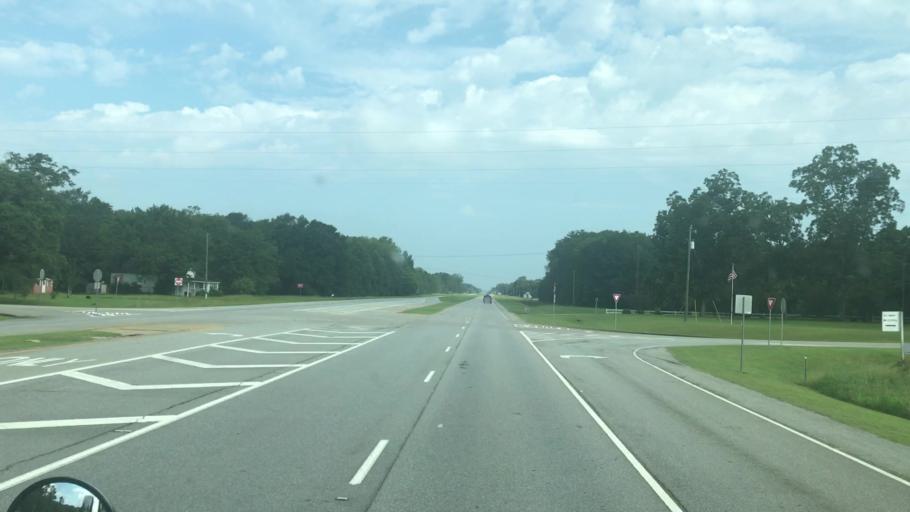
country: US
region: Georgia
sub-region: Early County
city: Blakely
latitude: 31.2797
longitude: -84.8364
